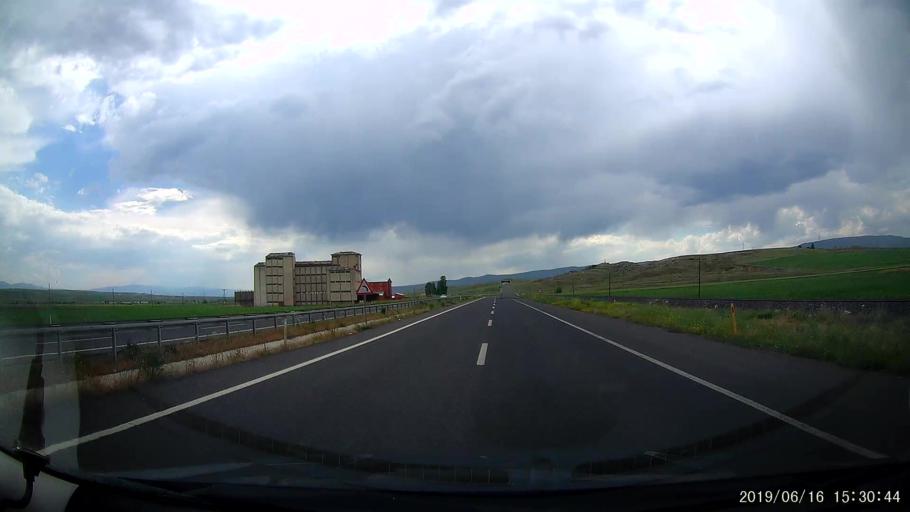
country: TR
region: Erzurum
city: Horasan
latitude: 40.0343
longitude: 42.0966
